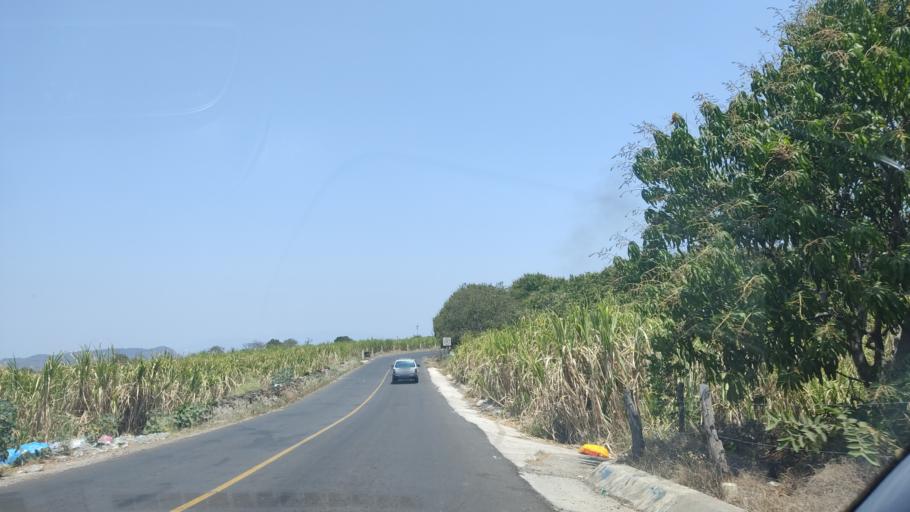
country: MX
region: Nayarit
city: Puga
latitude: 21.5703
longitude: -104.8258
